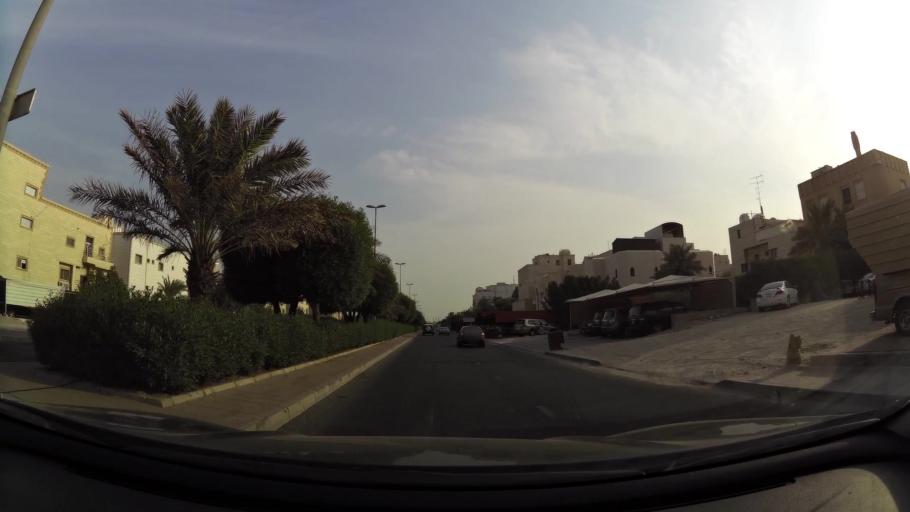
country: KW
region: Mubarak al Kabir
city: Mubarak al Kabir
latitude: 29.1895
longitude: 48.0707
